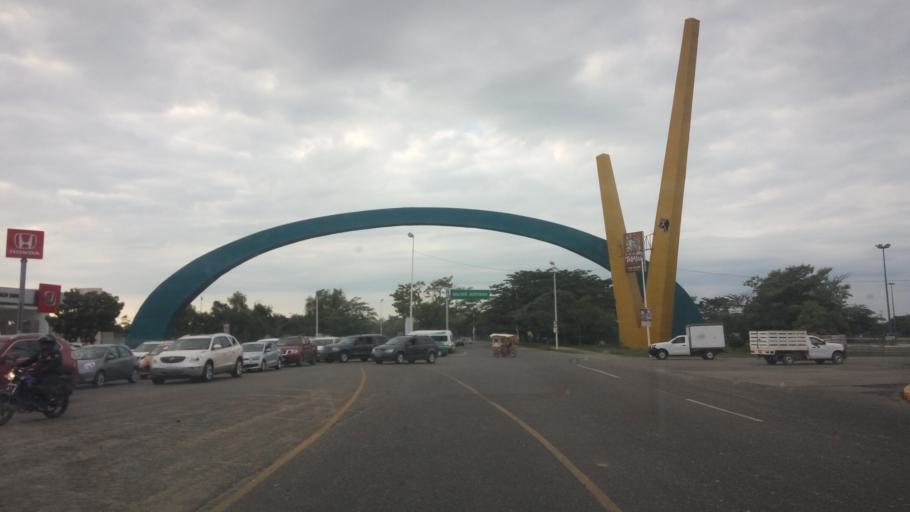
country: MX
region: Tabasco
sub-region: Nacajuca
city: Bosque de Saloya
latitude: 18.0037
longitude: -92.9598
